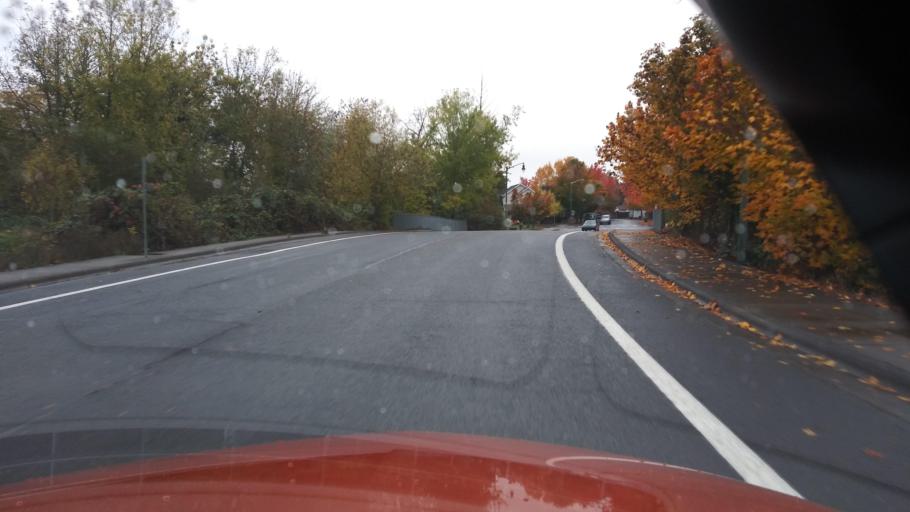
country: US
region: Oregon
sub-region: Washington County
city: Forest Grove
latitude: 45.5338
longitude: -123.1131
